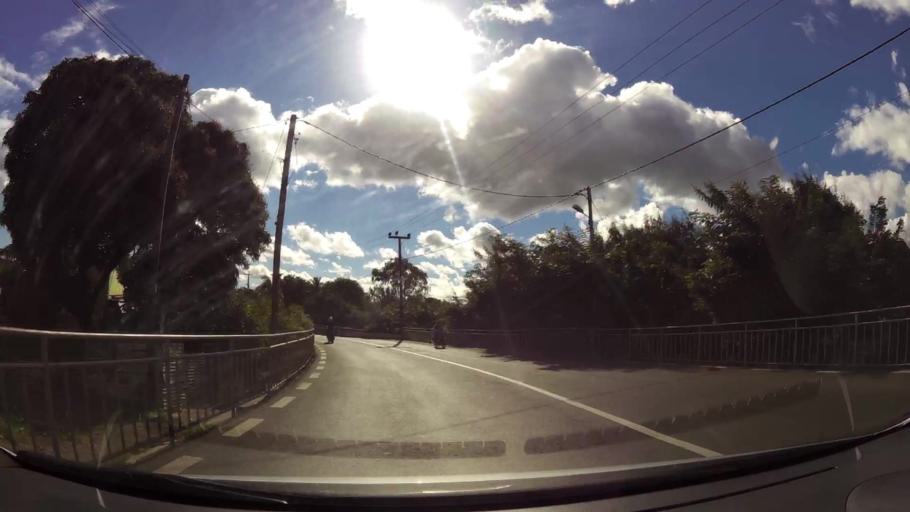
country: MU
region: Pamplemousses
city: Le Hochet
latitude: -20.1514
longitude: 57.5157
